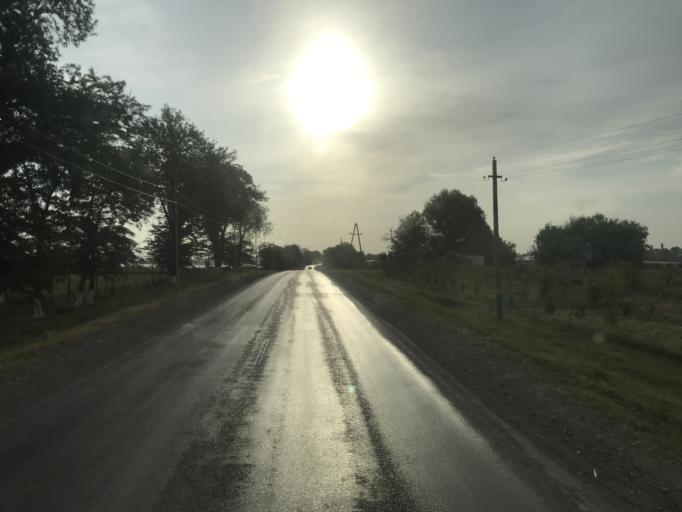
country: KZ
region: Ongtustik Qazaqstan
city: Saryaghash
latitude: 41.4921
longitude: 69.2926
